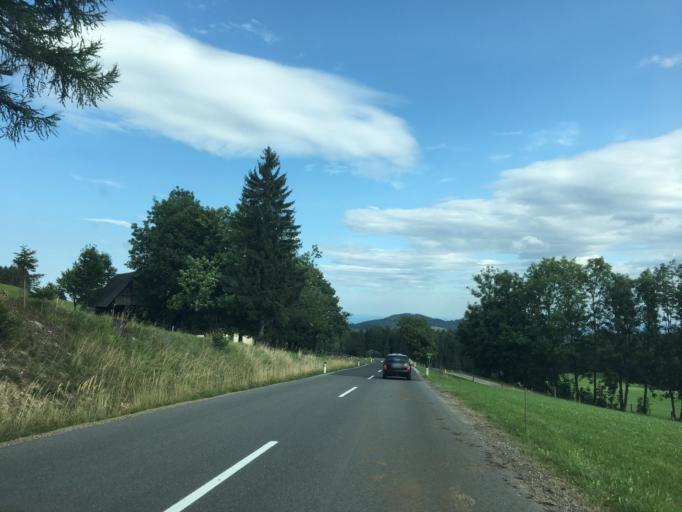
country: AT
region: Styria
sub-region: Politischer Bezirk Deutschlandsberg
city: Gressenberg
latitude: 46.8293
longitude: 15.0846
